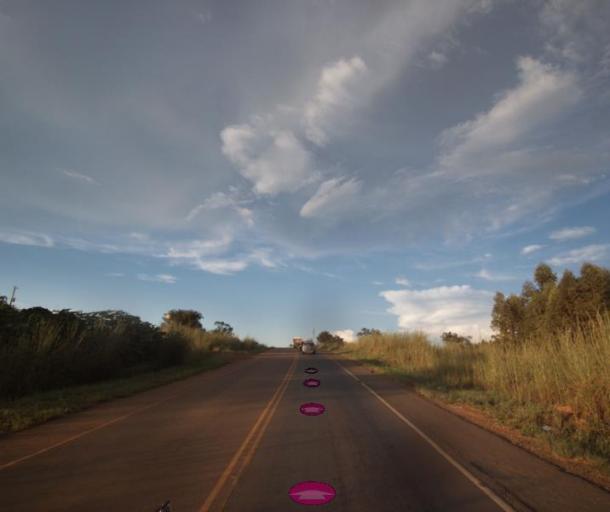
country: BR
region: Goias
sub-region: Anapolis
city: Anapolis
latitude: -16.2272
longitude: -48.9267
